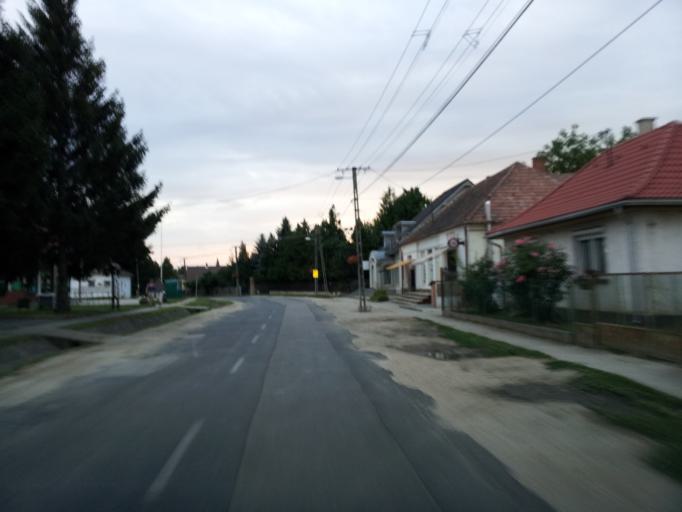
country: HU
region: Somogy
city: Adand
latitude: 46.8592
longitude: 18.1636
